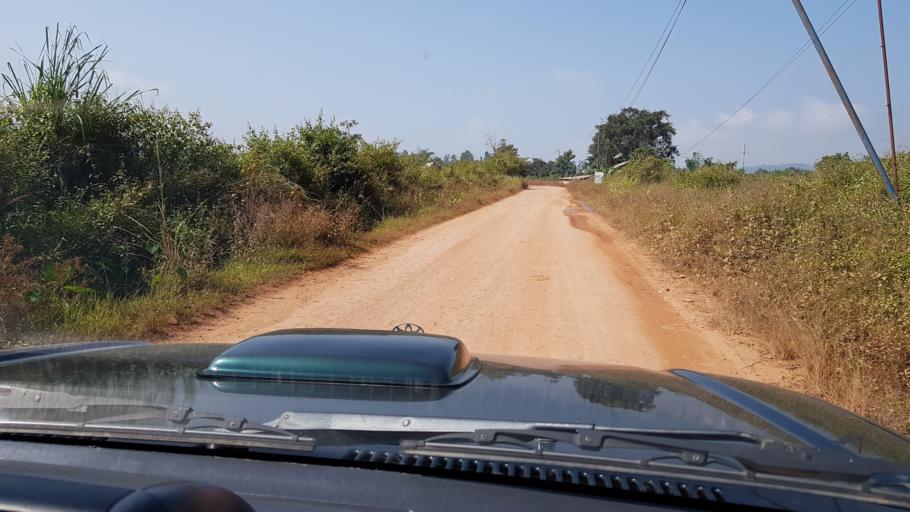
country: LA
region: Oudomxai
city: Muang Xay
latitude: 20.7177
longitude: 102.0431
